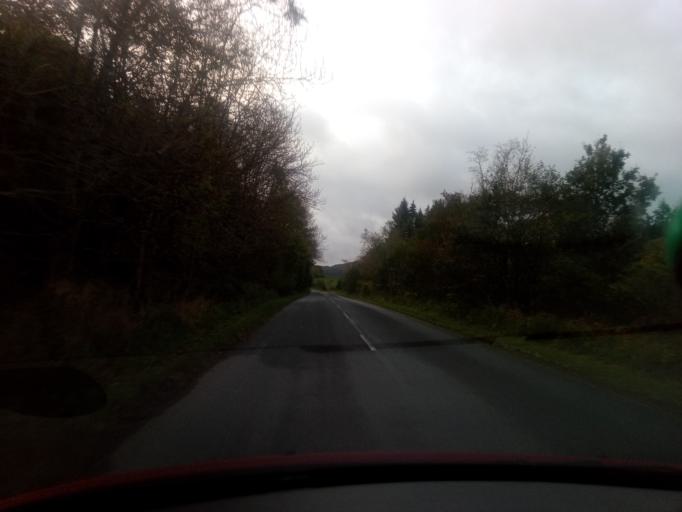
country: GB
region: Scotland
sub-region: The Scottish Borders
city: Hawick
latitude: 55.3562
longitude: -2.6483
